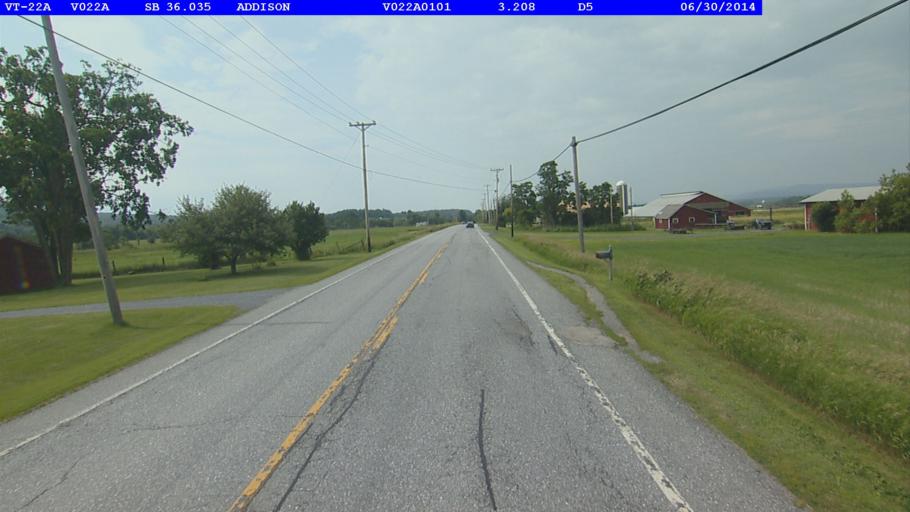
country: US
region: Vermont
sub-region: Addison County
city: Vergennes
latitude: 44.0757
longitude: -73.3037
